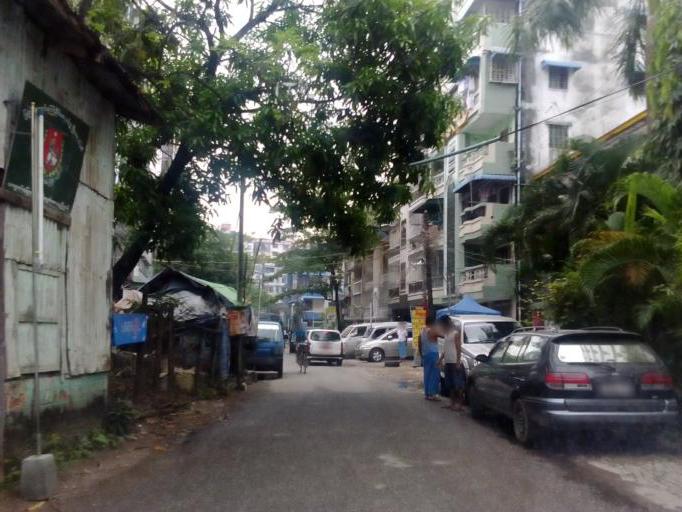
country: MM
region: Yangon
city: Yangon
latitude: 16.7996
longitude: 96.1776
